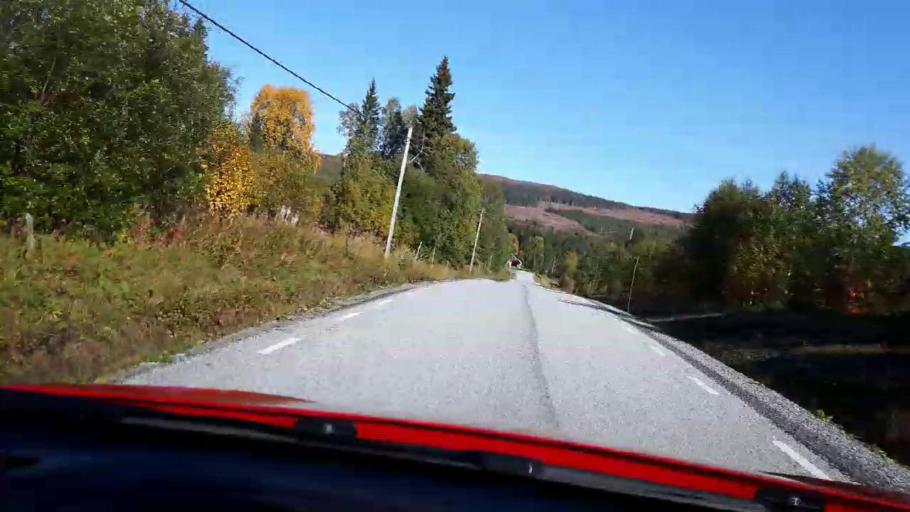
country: NO
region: Nord-Trondelag
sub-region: Royrvik
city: Royrvik
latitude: 64.7306
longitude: 13.9989
